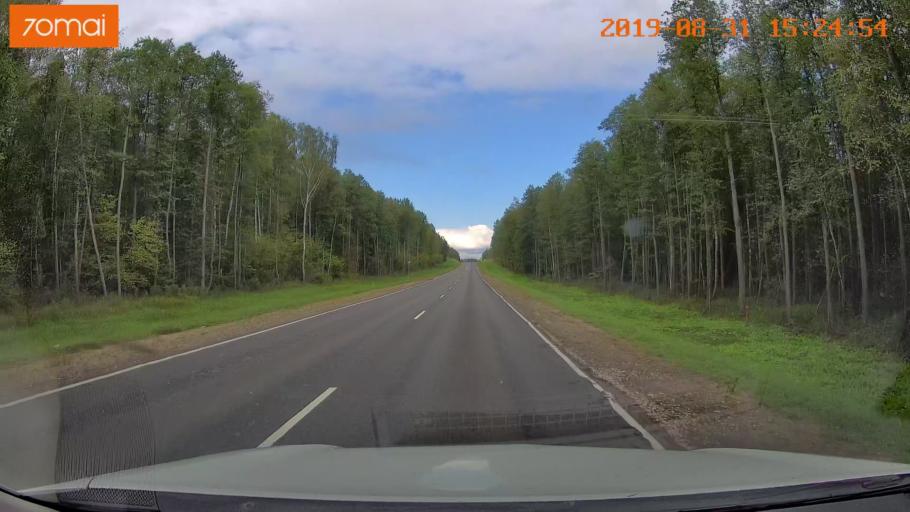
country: RU
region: Kaluga
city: Baryatino
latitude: 54.5341
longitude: 34.5117
